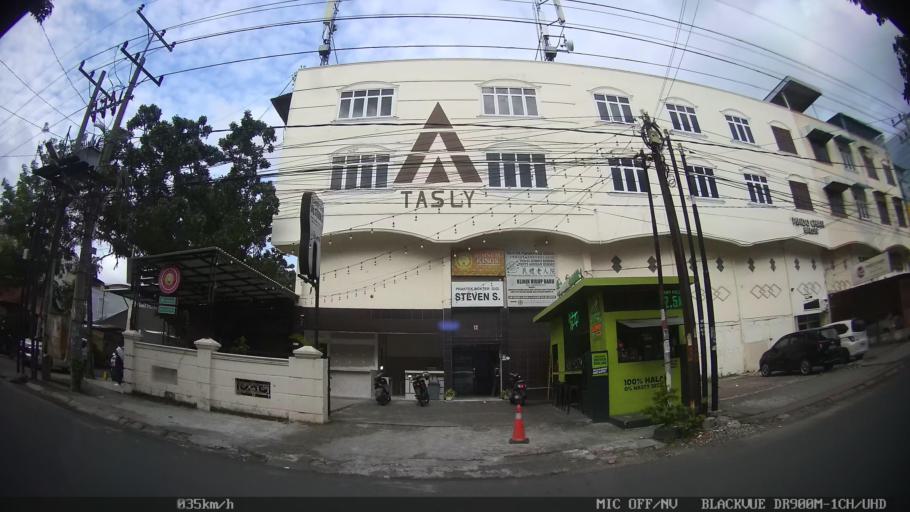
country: ID
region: North Sumatra
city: Medan
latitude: 3.5980
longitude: 98.6780
